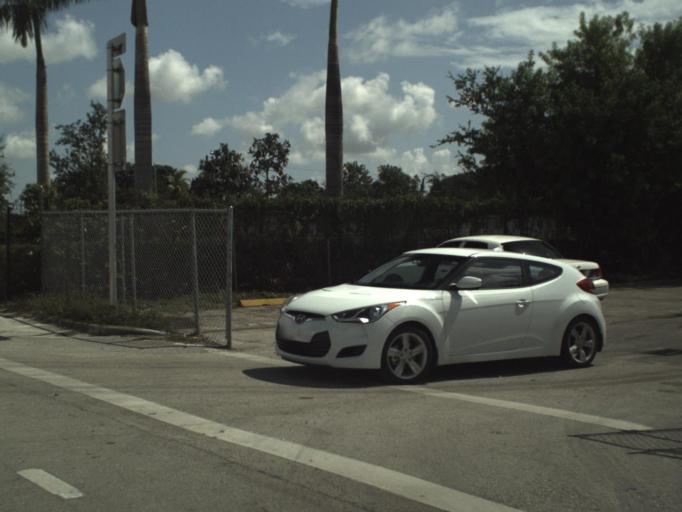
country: US
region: Florida
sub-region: Broward County
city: Miami Gardens
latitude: 25.9820
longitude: -80.2064
